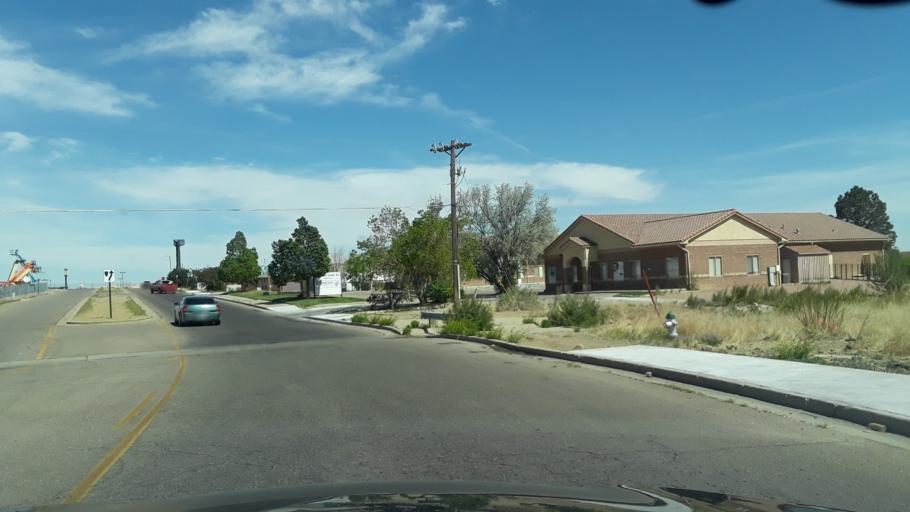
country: US
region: Colorado
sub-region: Pueblo County
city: Pueblo
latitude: 38.3118
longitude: -104.6181
